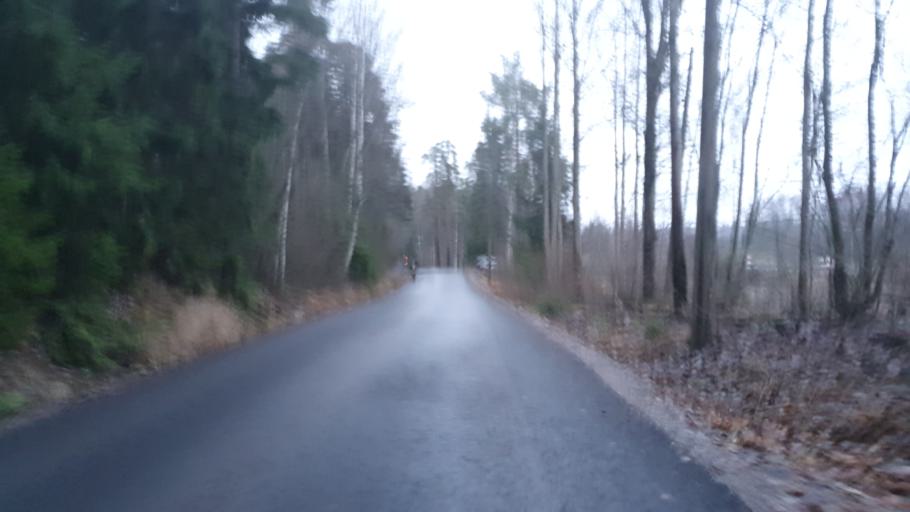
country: FI
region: Uusimaa
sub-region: Helsinki
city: Kilo
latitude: 60.2711
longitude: 24.7671
